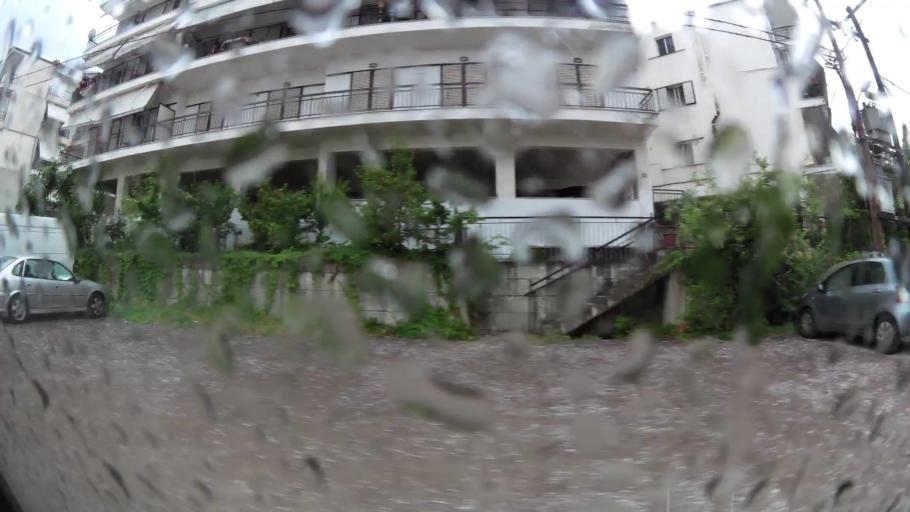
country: GR
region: Central Macedonia
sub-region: Nomos Imathias
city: Veroia
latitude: 40.5260
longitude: 22.1945
